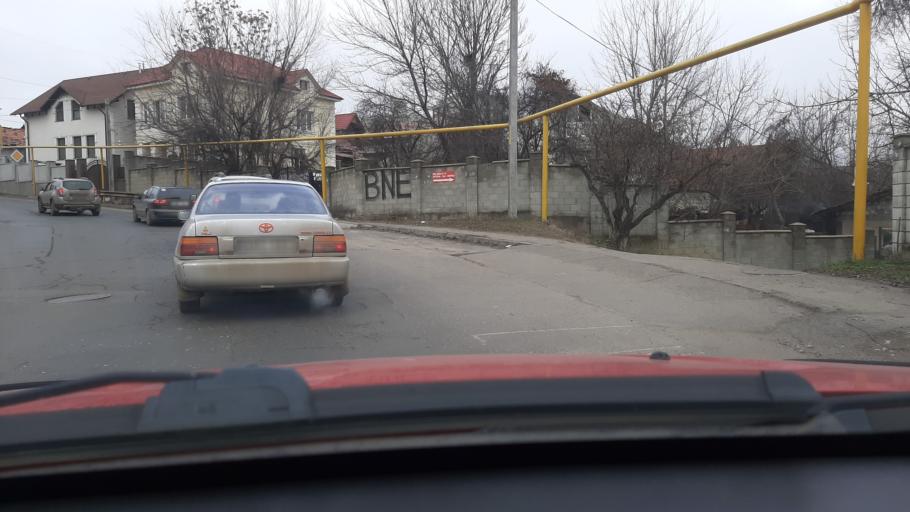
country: MD
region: Chisinau
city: Chisinau
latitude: 47.0077
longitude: 28.8403
